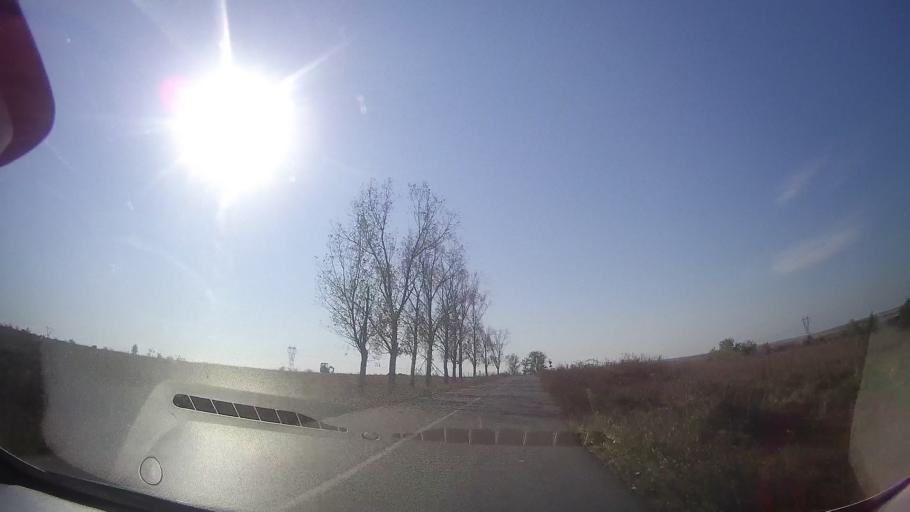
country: RO
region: Timis
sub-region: Comuna Topolovatu Mare
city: Topolovatu Mare
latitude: 45.8112
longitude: 21.5835
